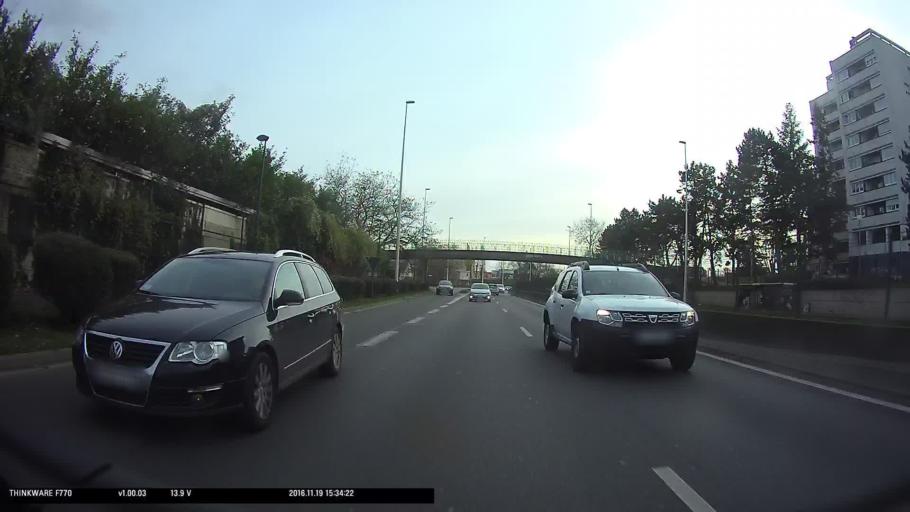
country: FR
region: Ile-de-France
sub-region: Departement du Val-d'Oise
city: Cergy-Pontoise
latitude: 49.0501
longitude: 2.0816
